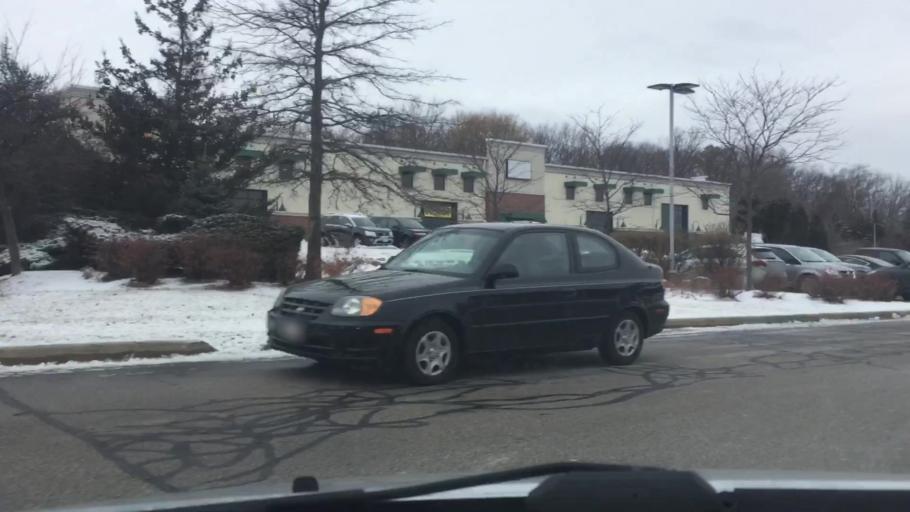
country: US
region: Wisconsin
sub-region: Waukesha County
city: Butler
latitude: 43.0895
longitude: -88.0753
